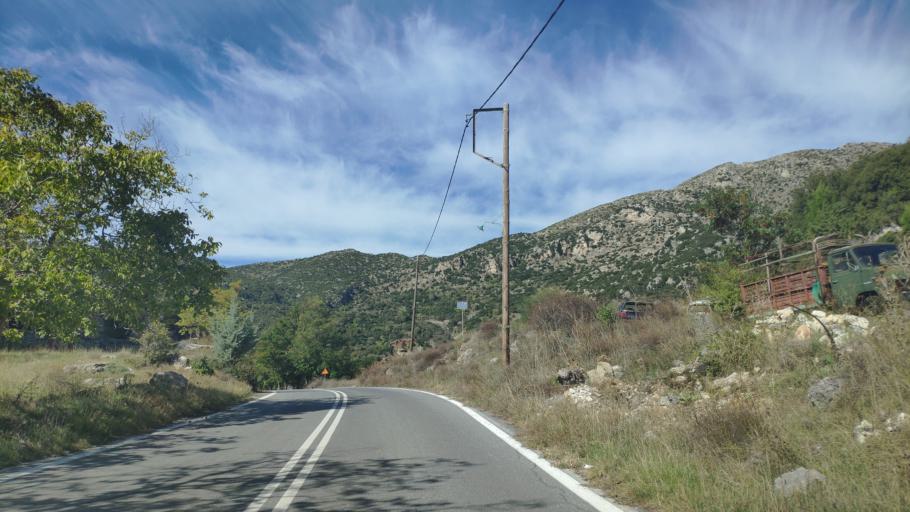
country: GR
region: Peloponnese
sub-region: Nomos Arkadias
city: Dimitsana
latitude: 37.5528
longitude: 22.0863
